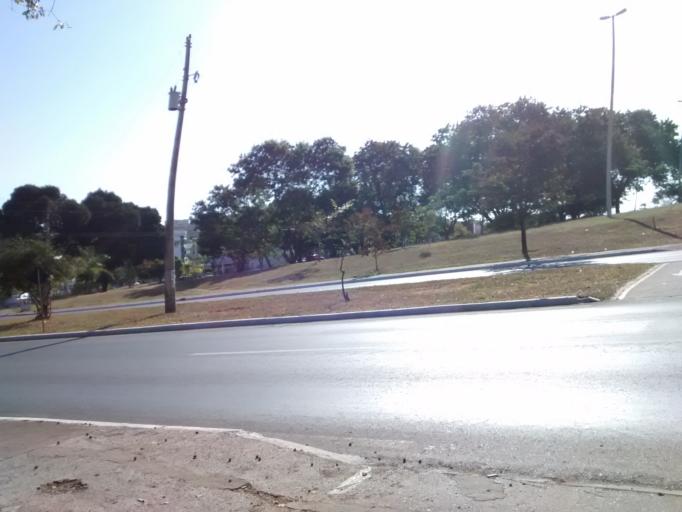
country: BR
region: Federal District
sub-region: Brasilia
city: Brasilia
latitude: -15.8037
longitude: -47.9298
